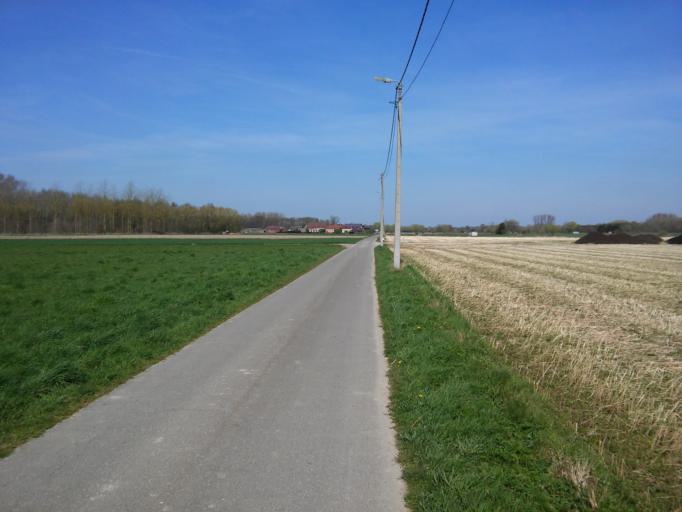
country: BE
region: Flanders
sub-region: Provincie Vlaams-Brabant
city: Kampenhout
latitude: 50.9592
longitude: 4.5527
